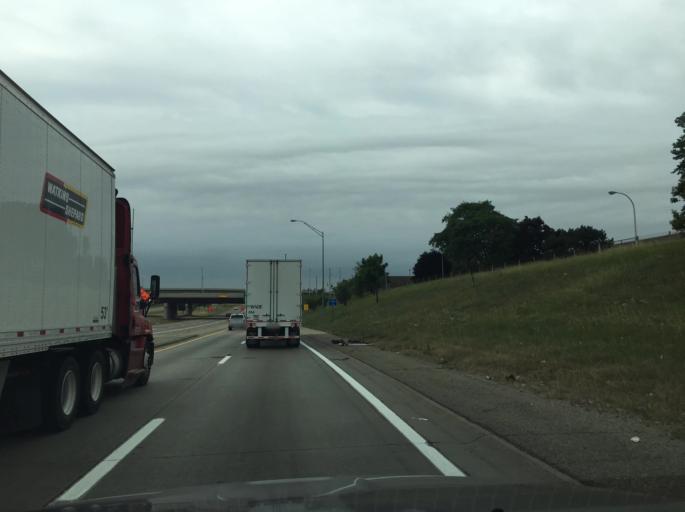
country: US
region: Michigan
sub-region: Macomb County
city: Center Line
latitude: 42.4934
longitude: -83.0464
